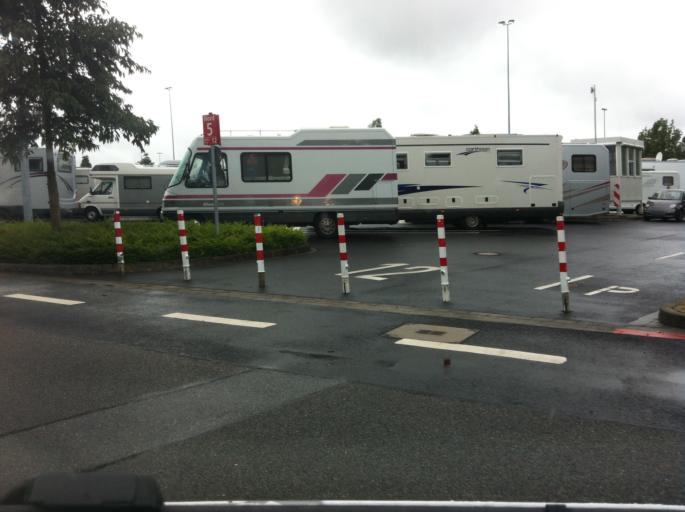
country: DE
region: North Rhine-Westphalia
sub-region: Regierungsbezirk Dusseldorf
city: Meerbusch
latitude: 51.2703
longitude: 6.7213
